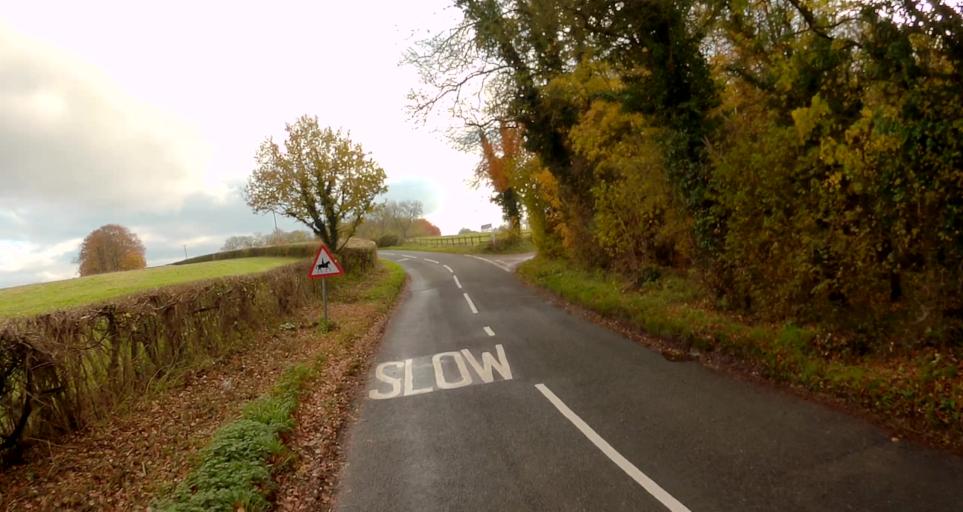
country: GB
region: England
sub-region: Hampshire
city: Old Basing
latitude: 51.2403
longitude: -1.0379
